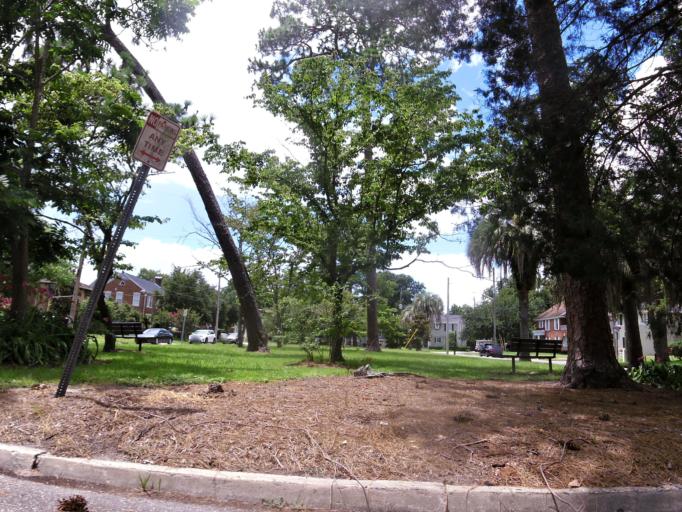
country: US
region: Florida
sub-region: Duval County
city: Jacksonville
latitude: 30.3047
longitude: -81.7026
